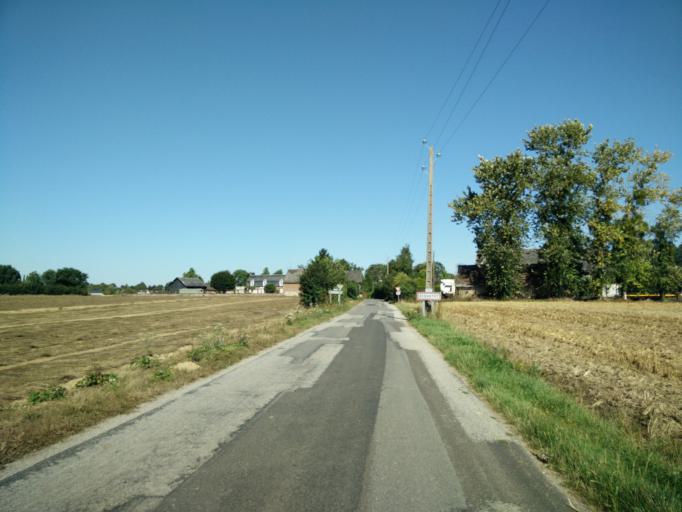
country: FR
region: Haute-Normandie
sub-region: Departement de l'Eure
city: La Haye-Malherbe
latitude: 49.1660
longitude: 1.0199
